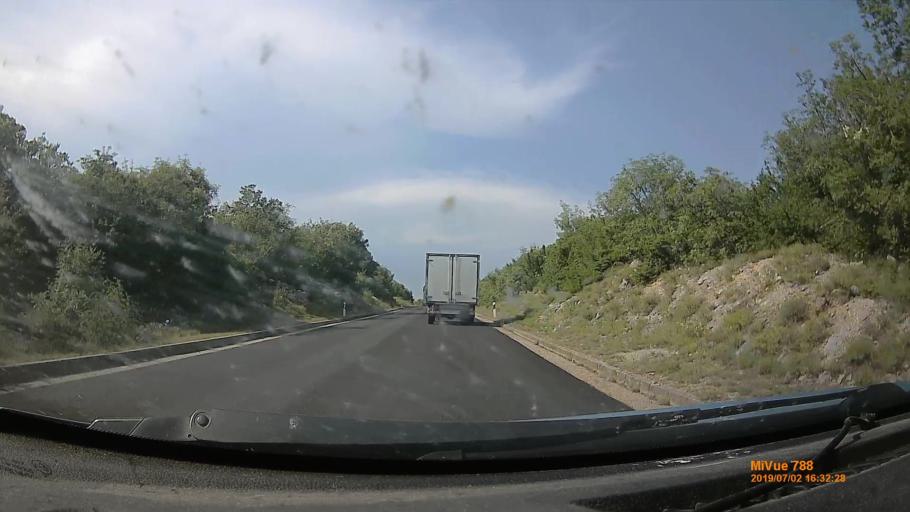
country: HR
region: Primorsko-Goranska
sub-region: Grad Krk
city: Krk
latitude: 45.0654
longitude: 14.4881
